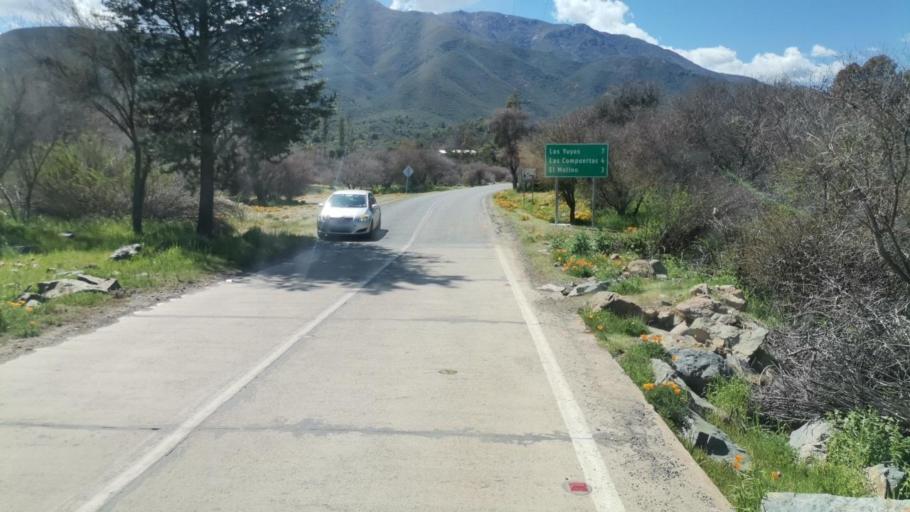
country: CL
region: Valparaiso
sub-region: Provincia de Marga Marga
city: Limache
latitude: -33.1757
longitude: -71.1693
